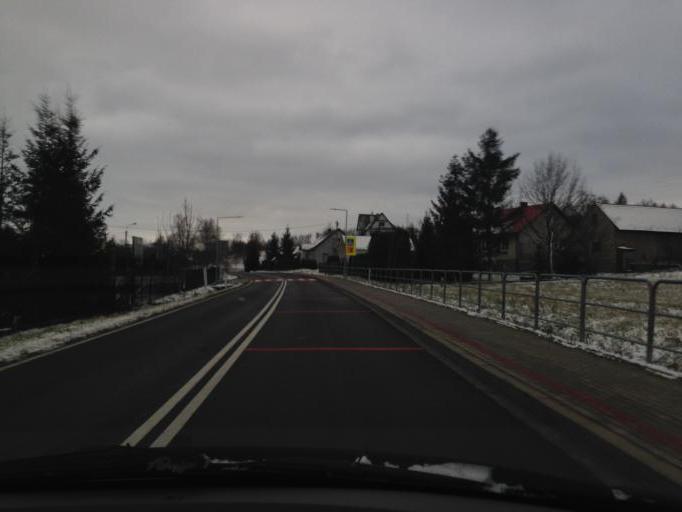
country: PL
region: Lesser Poland Voivodeship
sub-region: Powiat tarnowski
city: Gromnik
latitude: 49.8358
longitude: 20.9875
